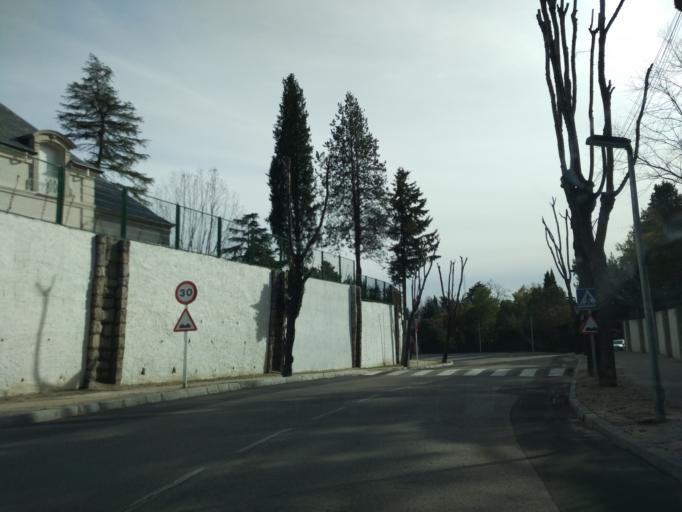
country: ES
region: Madrid
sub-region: Provincia de Madrid
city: Tetuan de las Victorias
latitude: 40.4629
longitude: -3.7292
